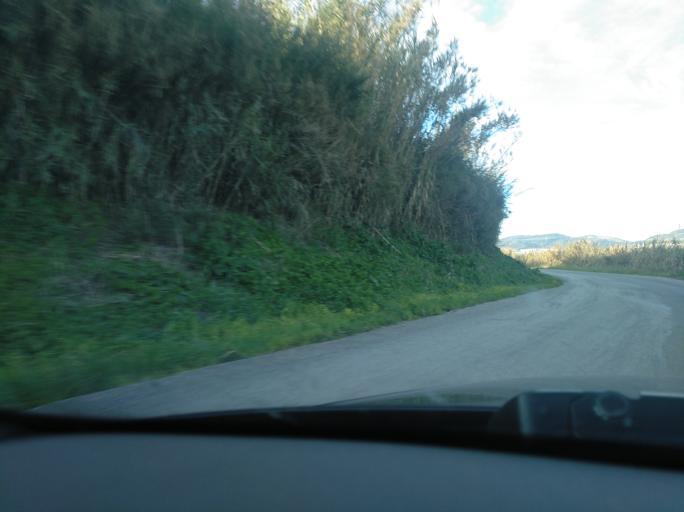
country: PT
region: Lisbon
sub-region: Loures
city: Unhos
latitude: 38.8329
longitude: -9.1210
